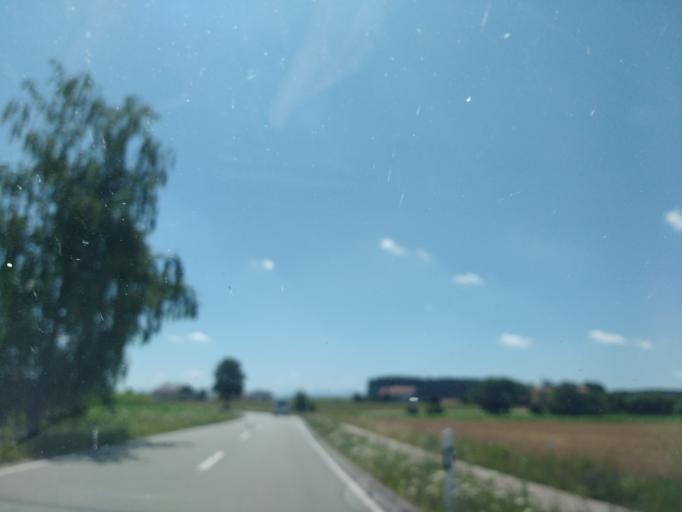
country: DE
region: Bavaria
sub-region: Upper Bavaria
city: Kienberg
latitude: 48.0398
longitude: 12.4500
